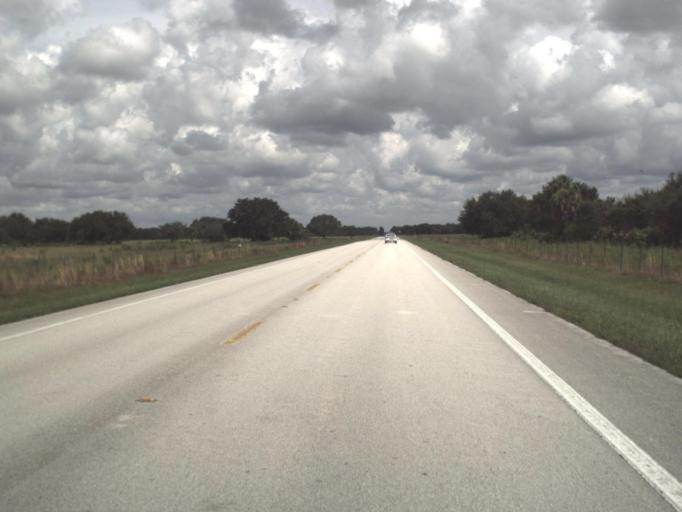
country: US
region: Florida
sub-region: Sarasota County
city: Warm Mineral Springs
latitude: 27.1935
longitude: -82.1700
